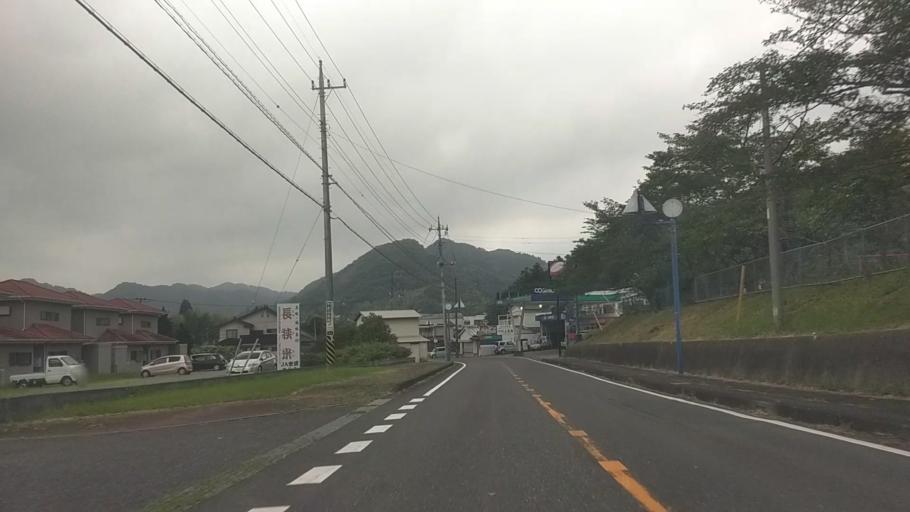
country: JP
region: Chiba
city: Kawaguchi
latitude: 35.1436
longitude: 139.9673
